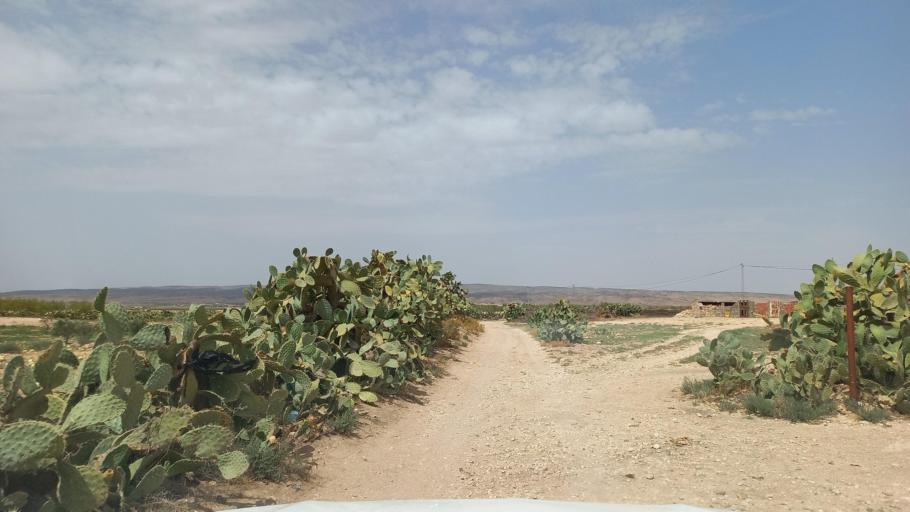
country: TN
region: Al Qasrayn
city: Kasserine
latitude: 35.2876
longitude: 9.0065
